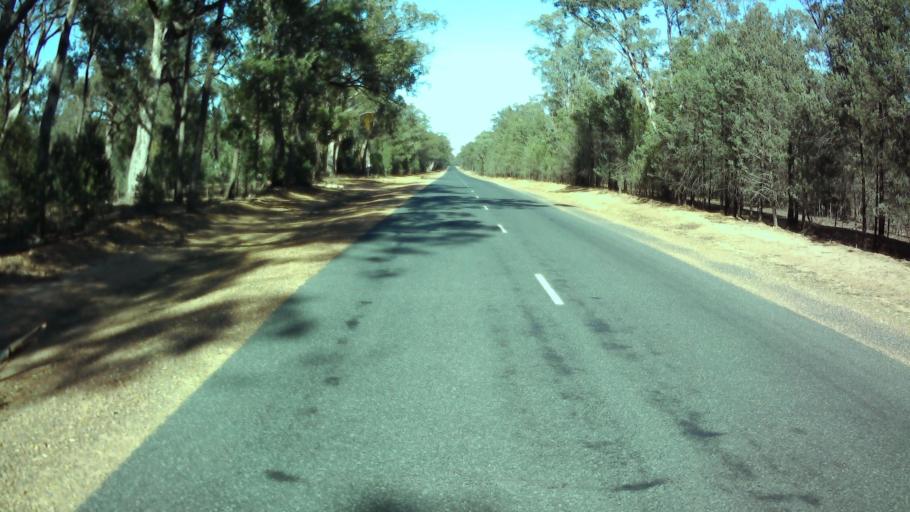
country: AU
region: New South Wales
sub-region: Weddin
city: Grenfell
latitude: -34.0241
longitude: 148.0210
